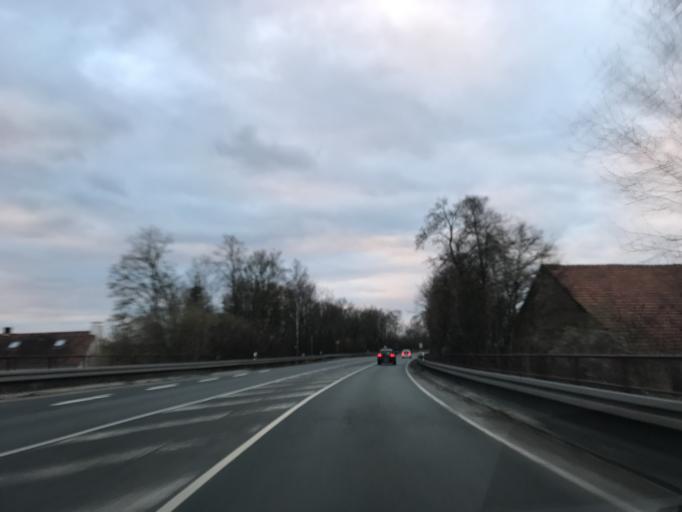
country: DE
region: Hesse
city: Grebenstein
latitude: 51.4276
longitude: 9.4353
